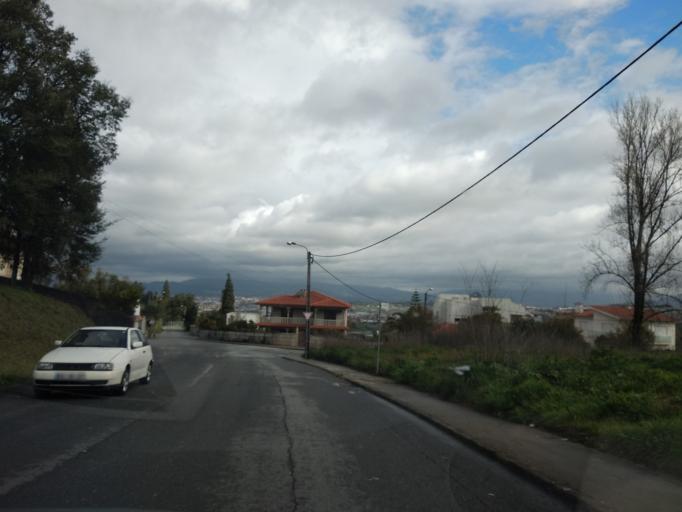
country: PT
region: Braga
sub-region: Braga
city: Braga
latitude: 41.5434
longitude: -8.4427
